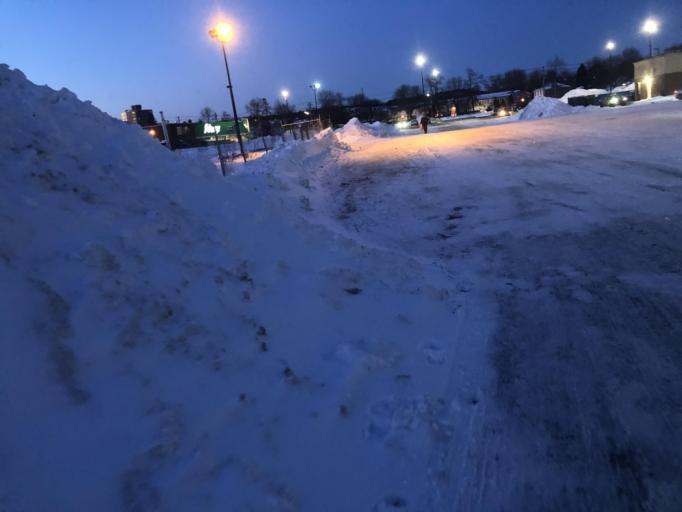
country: CA
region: New Brunswick
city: Saint John
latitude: 45.2783
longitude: -66.0776
